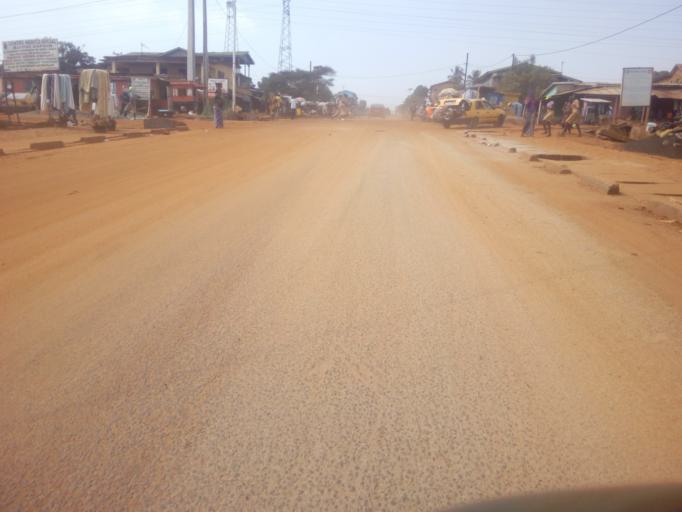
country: GN
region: Conakry
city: Conakry
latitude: 9.6346
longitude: -13.5725
